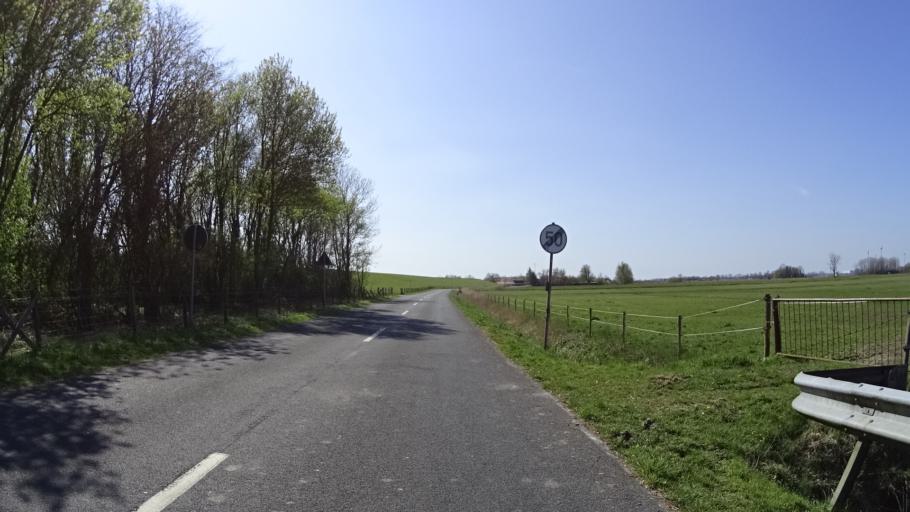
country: DE
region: Lower Saxony
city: Weener
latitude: 53.1985
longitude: 7.4036
